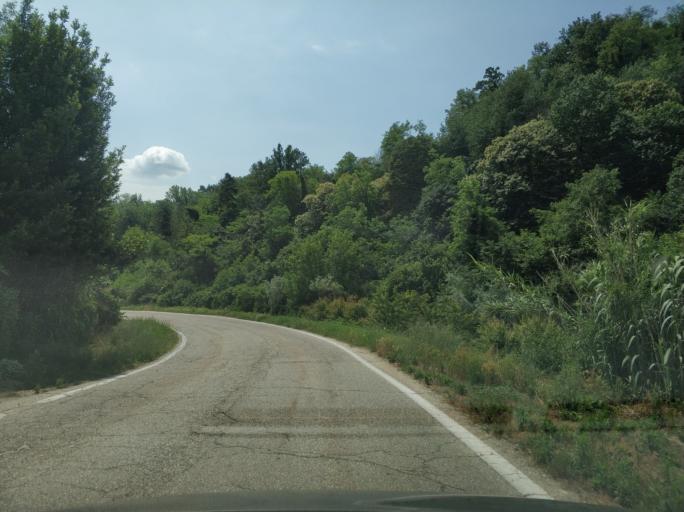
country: IT
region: Piedmont
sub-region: Provincia di Cuneo
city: Santo Stefano Roero
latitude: 44.7854
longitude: 7.9559
